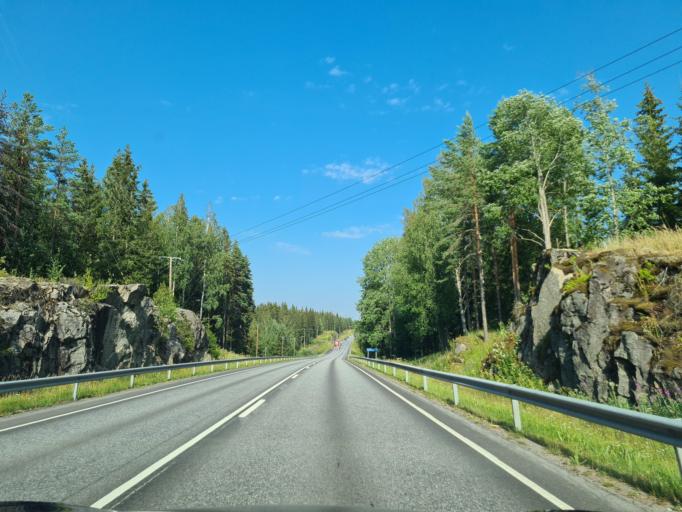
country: FI
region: Satakunta
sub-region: Pori
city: Laengelmaeki
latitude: 61.7853
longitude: 22.2208
